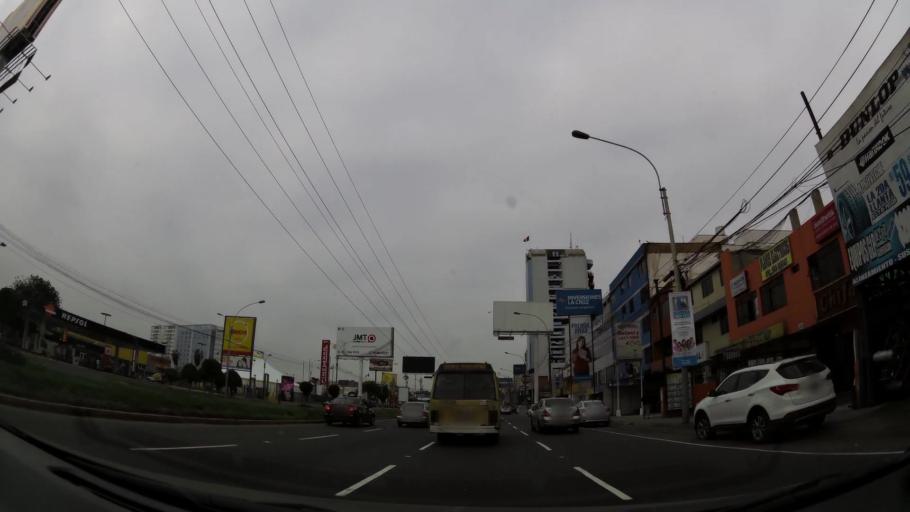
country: PE
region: Callao
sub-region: Callao
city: Callao
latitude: -12.0781
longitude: -77.0902
